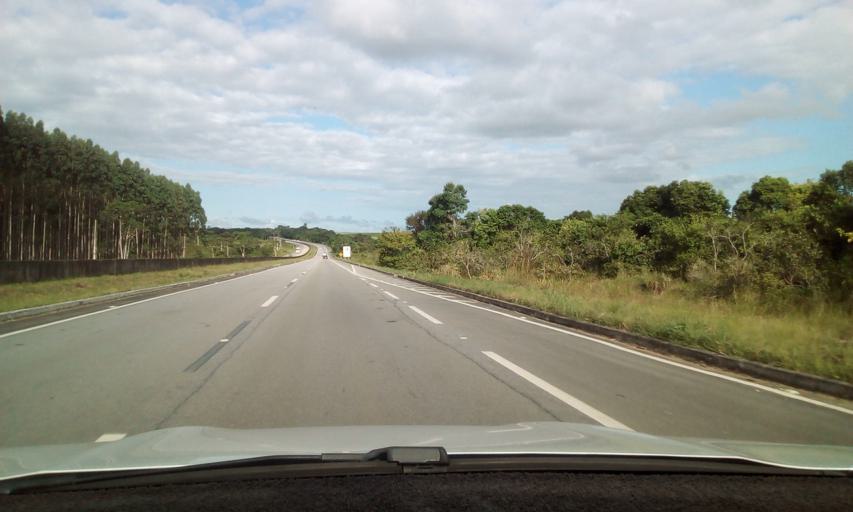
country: BR
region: Paraiba
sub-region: Santa Rita
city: Santa Rita
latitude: -7.0490
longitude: -35.0421
